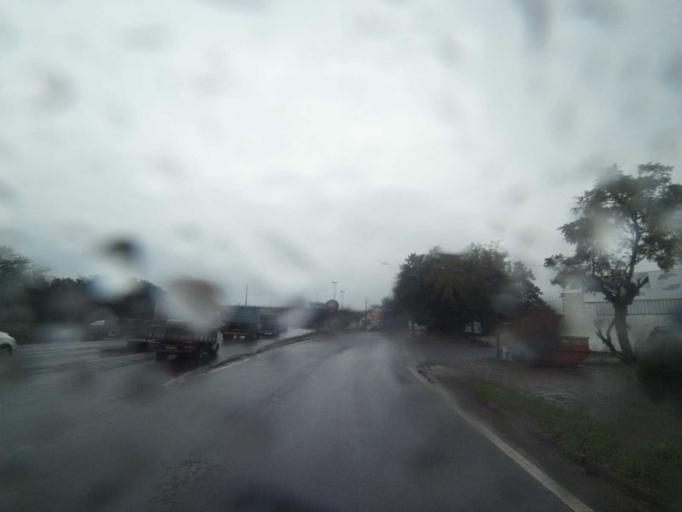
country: BR
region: Rio Grande do Sul
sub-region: Sao Leopoldo
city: Sao Leopoldo
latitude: -29.7623
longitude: -51.1525
